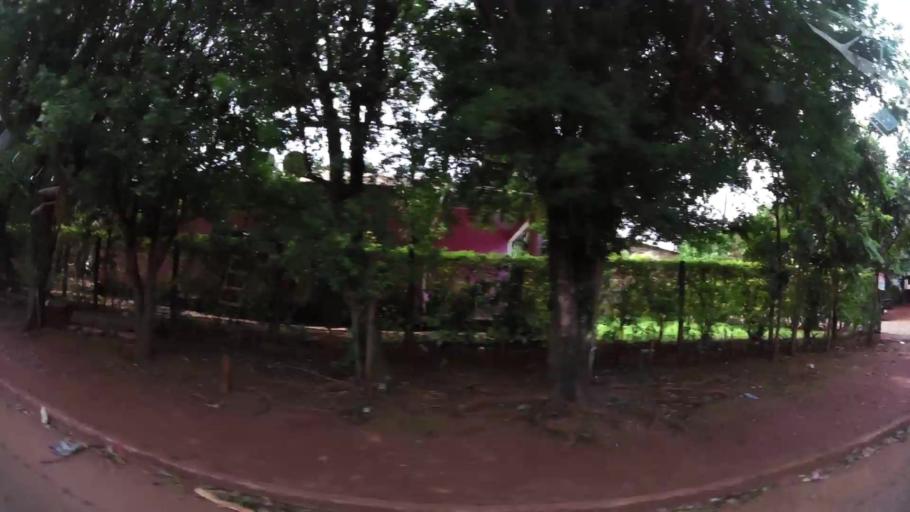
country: PY
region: Alto Parana
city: Ciudad del Este
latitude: -25.5003
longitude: -54.6251
